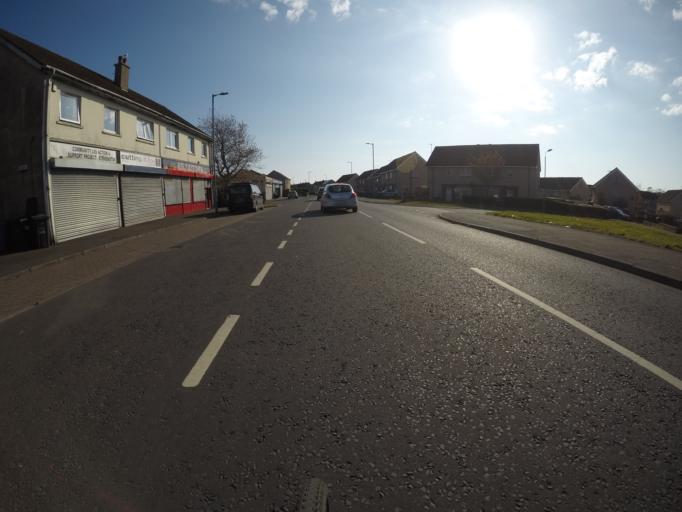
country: GB
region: Scotland
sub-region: North Ayrshire
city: Stevenston
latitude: 55.6491
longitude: -4.7443
